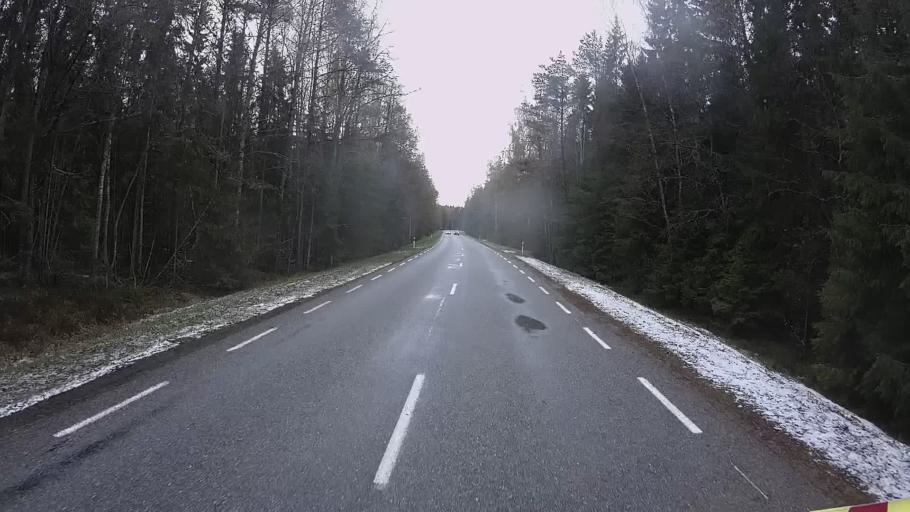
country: EE
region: Hiiumaa
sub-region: Kaerdla linn
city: Kardla
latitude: 59.0426
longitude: 22.6816
